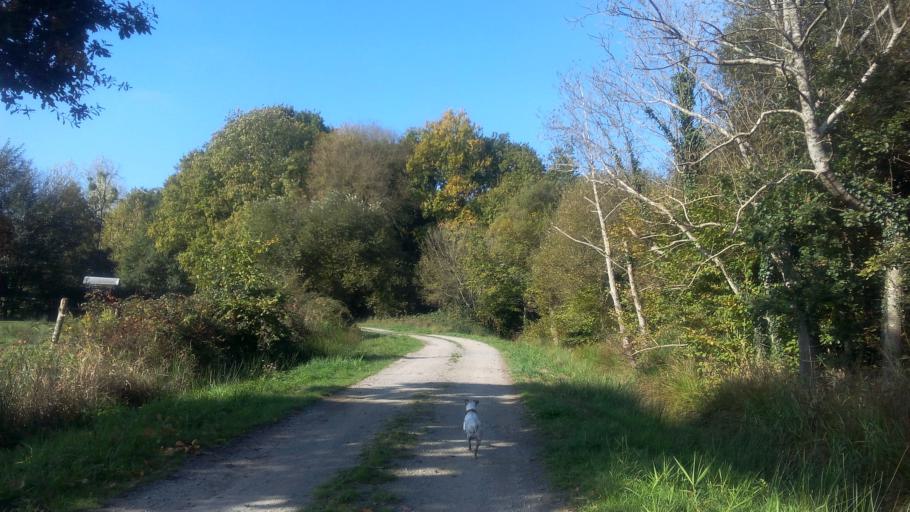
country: FR
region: Brittany
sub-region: Departement du Morbihan
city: Saint-Jean-la-Poterie
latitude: 47.6517
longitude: -2.1189
